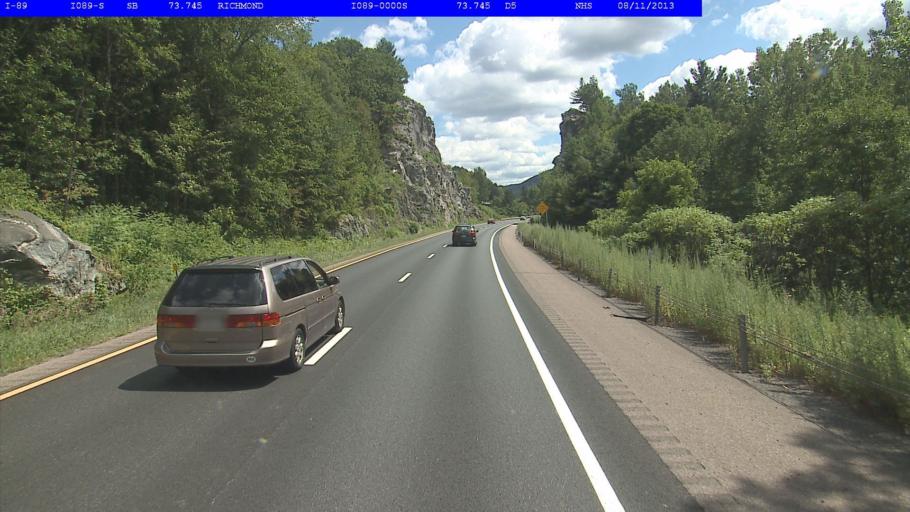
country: US
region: Vermont
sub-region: Chittenden County
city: Jericho
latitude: 44.3869
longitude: -72.9388
